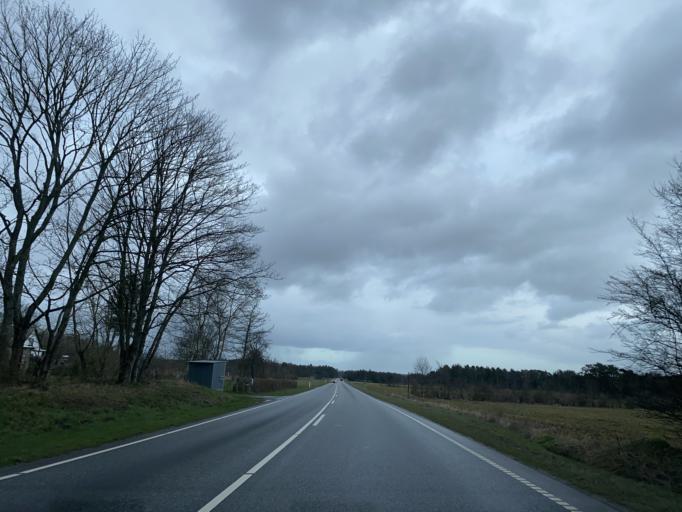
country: DK
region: Central Jutland
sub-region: Viborg Kommune
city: Bjerringbro
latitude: 56.2852
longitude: 9.6484
